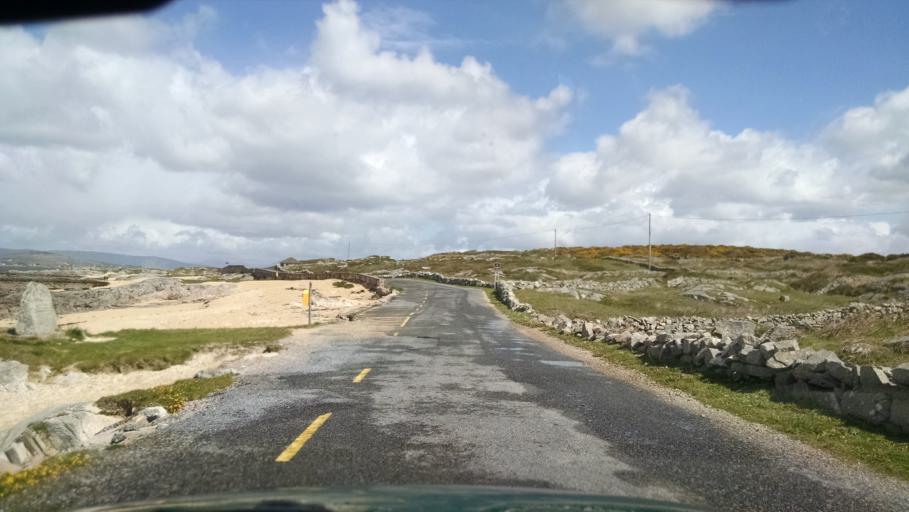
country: IE
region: Connaught
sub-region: County Galway
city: Oughterard
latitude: 53.2469
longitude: -9.6287
